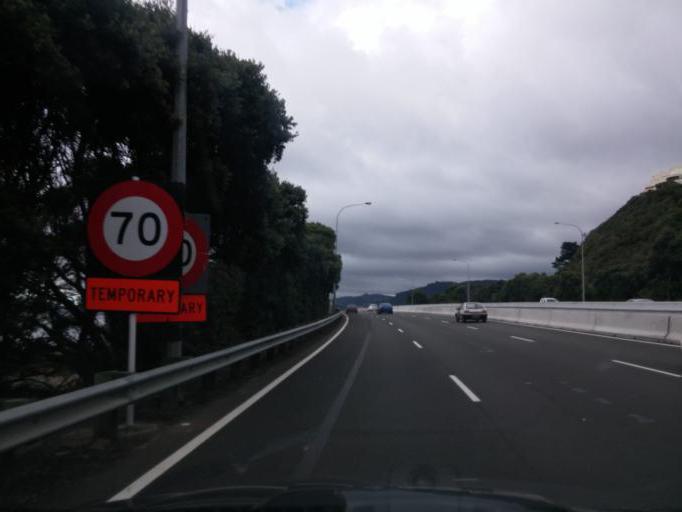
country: NZ
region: Wellington
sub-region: Wellington City
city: Wellington
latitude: -41.2512
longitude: 174.8079
